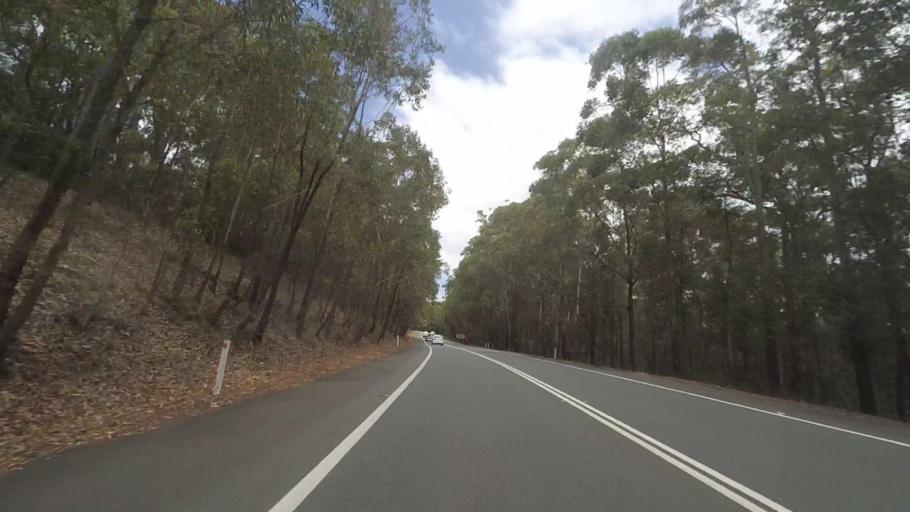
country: AU
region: New South Wales
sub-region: Shoalhaven Shire
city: Milton
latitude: -35.1606
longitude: 150.4476
